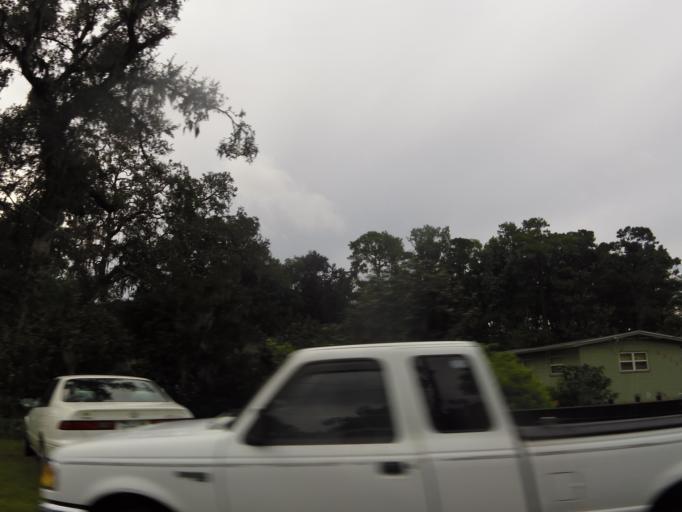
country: US
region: Florida
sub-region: Duval County
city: Jacksonville
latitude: 30.2959
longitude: -81.5966
